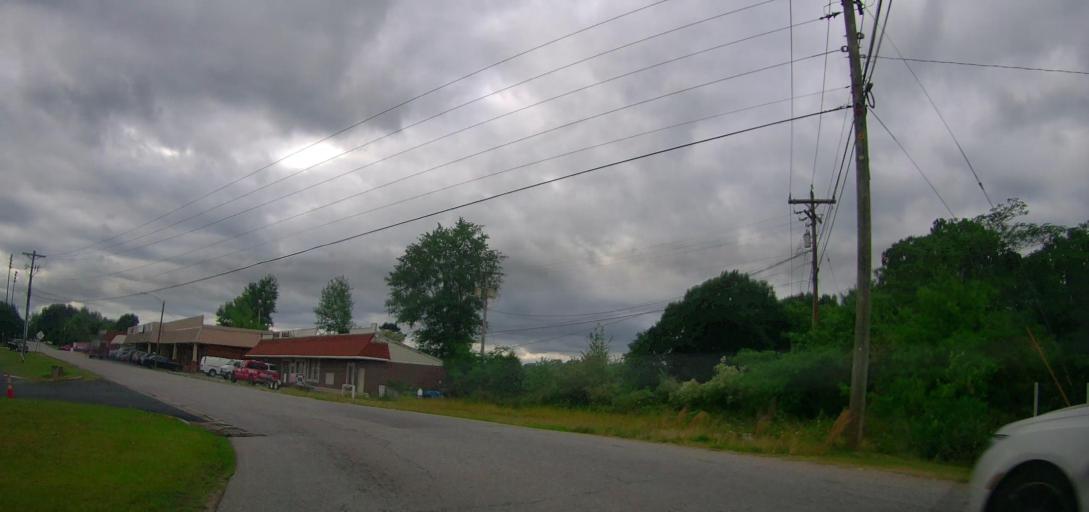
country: US
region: Georgia
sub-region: Walton County
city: Monroe
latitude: 33.8039
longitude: -83.7013
